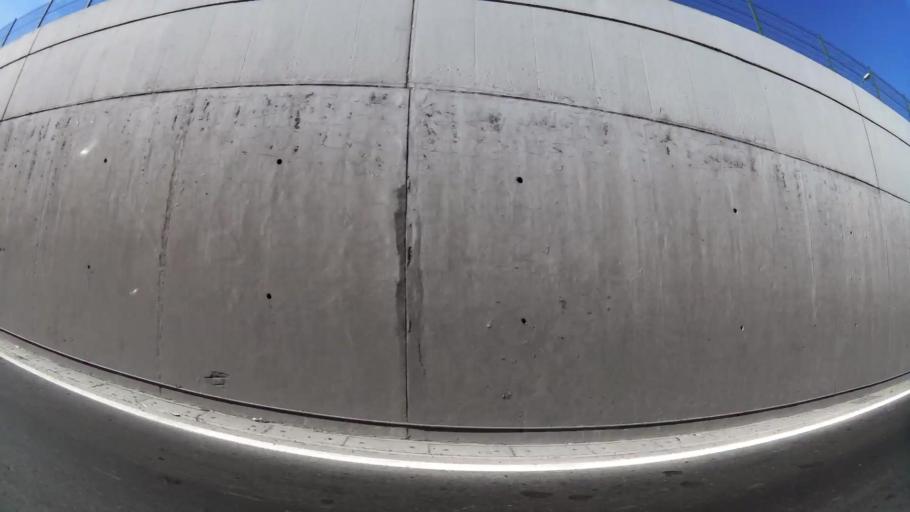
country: CL
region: Santiago Metropolitan
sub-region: Provincia de Santiago
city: Lo Prado
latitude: -33.4981
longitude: -70.7442
